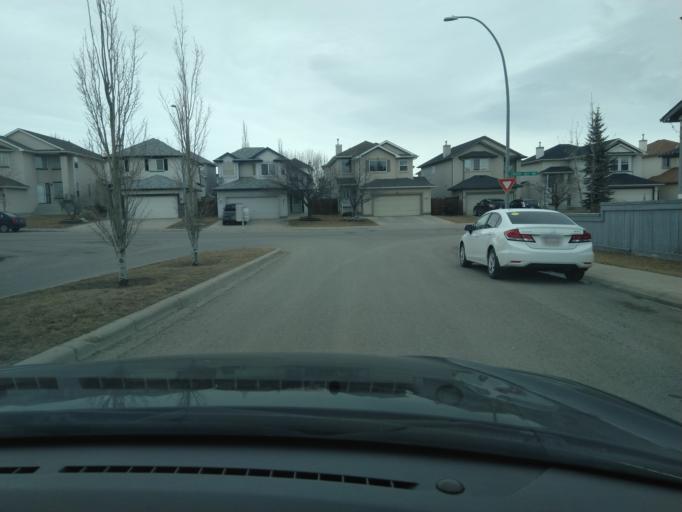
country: CA
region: Alberta
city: Calgary
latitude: 51.1712
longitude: -114.0460
